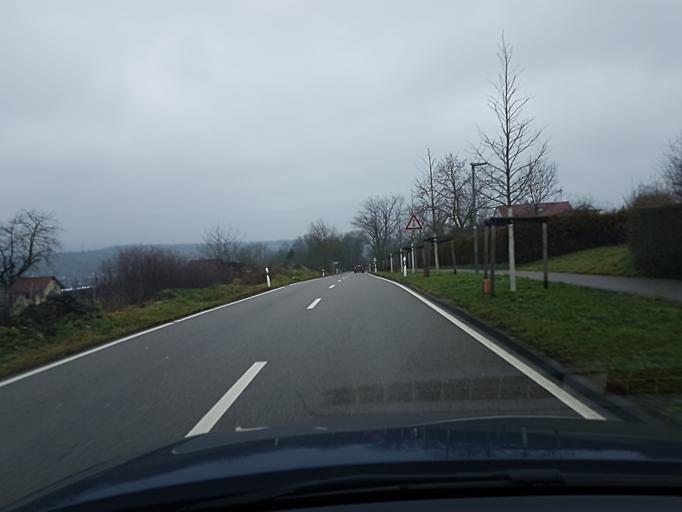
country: DE
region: Baden-Wuerttemberg
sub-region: Regierungsbezirk Stuttgart
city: Besigheim
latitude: 48.9898
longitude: 9.1543
